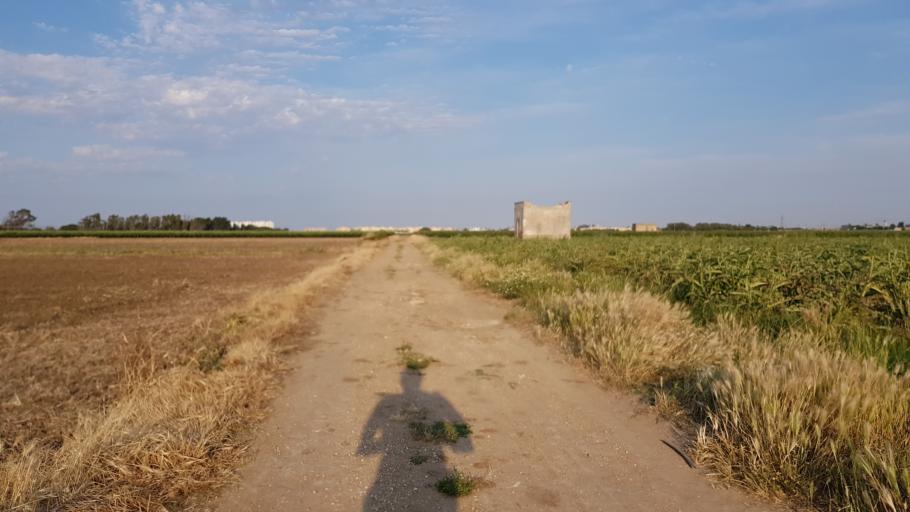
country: IT
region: Apulia
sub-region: Provincia di Brindisi
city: Brindisi
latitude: 40.6244
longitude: 17.8874
